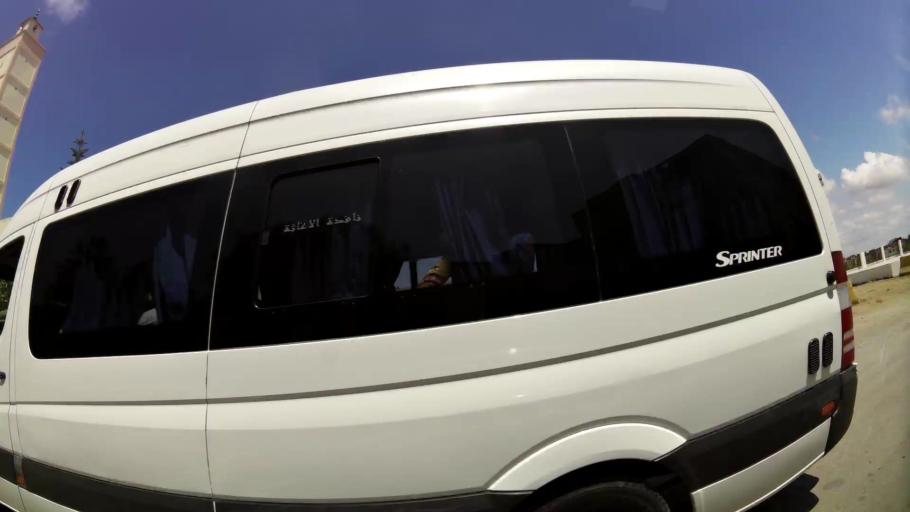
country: MA
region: Gharb-Chrarda-Beni Hssen
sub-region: Kenitra Province
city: Kenitra
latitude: 34.2603
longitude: -6.5516
